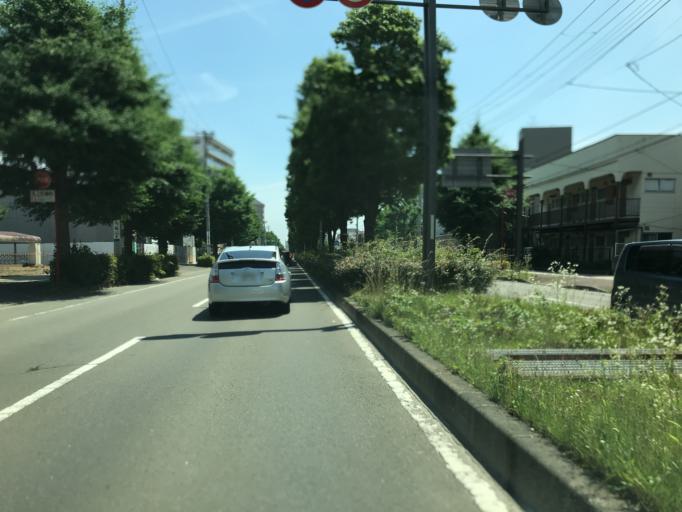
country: JP
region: Miyagi
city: Sendai-shi
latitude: 38.2732
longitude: 140.8747
